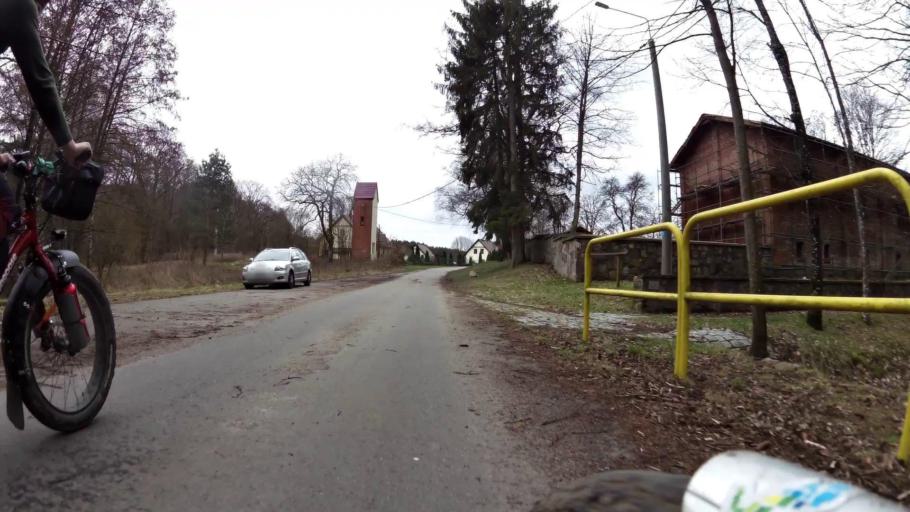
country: PL
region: Pomeranian Voivodeship
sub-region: Powiat bytowski
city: Trzebielino
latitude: 54.1406
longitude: 17.1496
